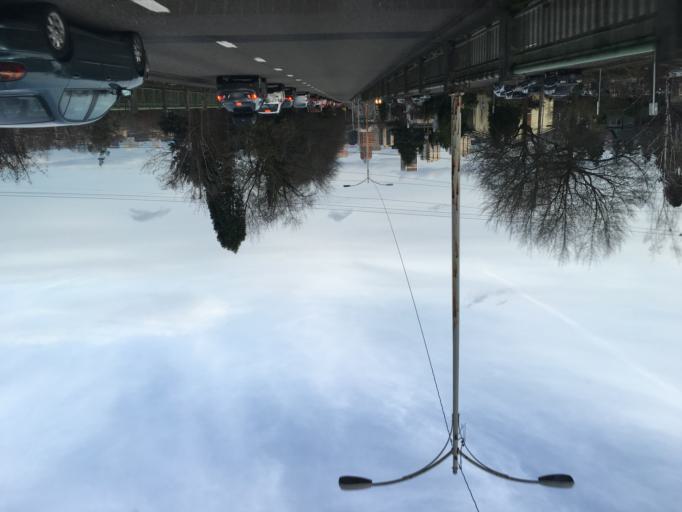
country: US
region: Oregon
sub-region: Multnomah County
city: Portland
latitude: 45.4970
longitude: -122.6779
